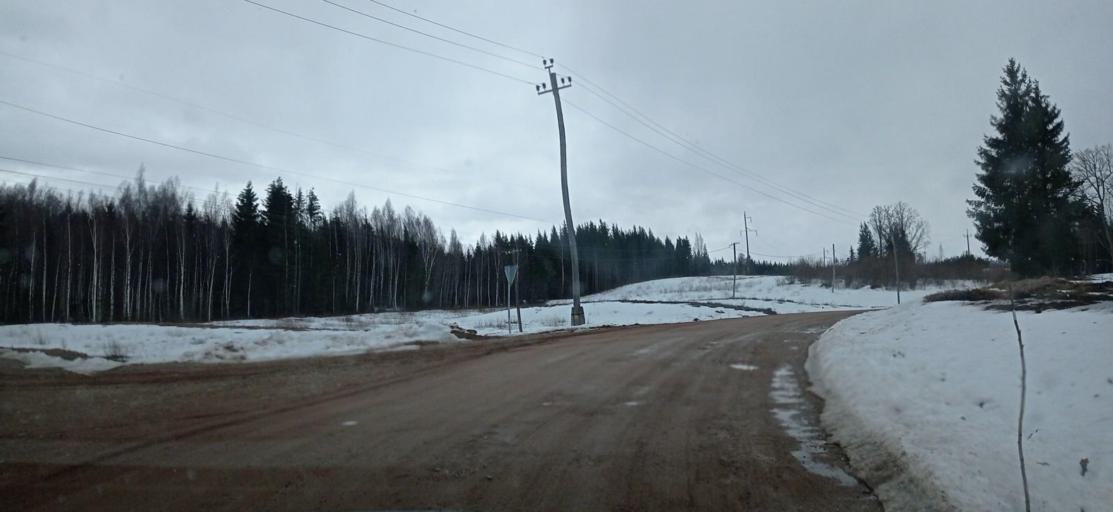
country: EE
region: Tartu
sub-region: UElenurme vald
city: Ulenurme
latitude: 58.1244
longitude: 26.7008
